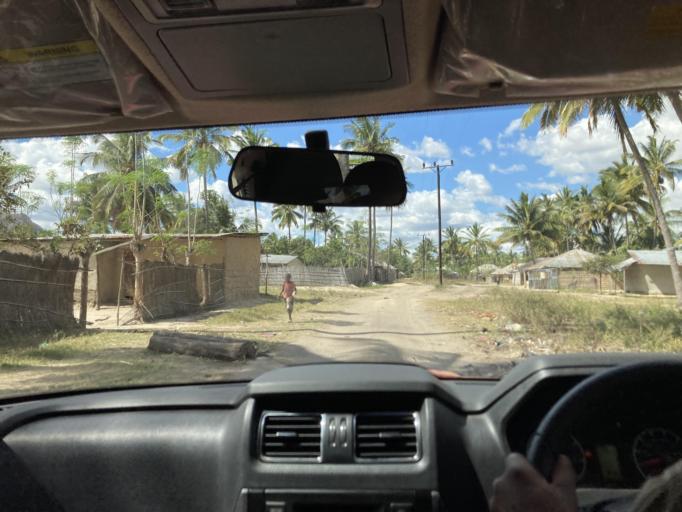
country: MZ
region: Cabo Delgado
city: Montepuez
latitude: -13.1319
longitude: 39.0153
